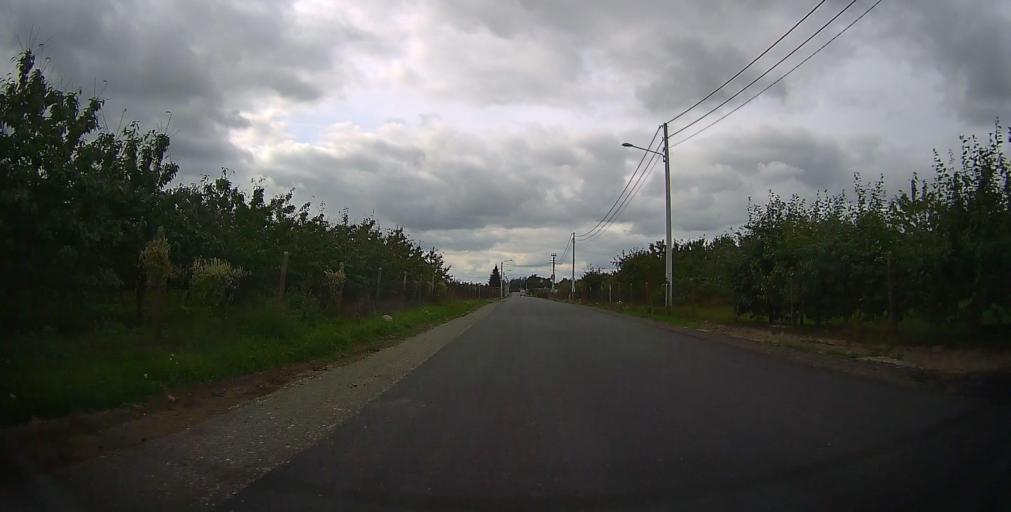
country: PL
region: Masovian Voivodeship
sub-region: Powiat grojecki
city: Belsk Duzy
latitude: 51.8105
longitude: 20.8396
